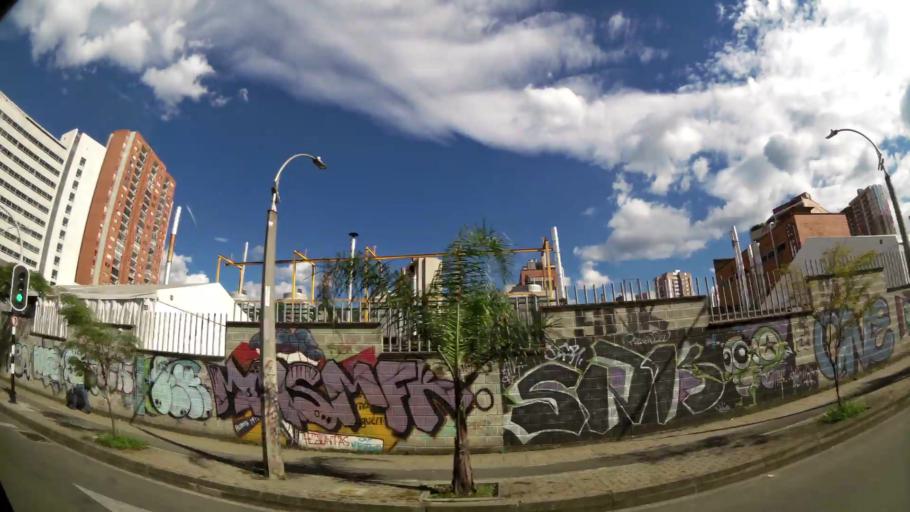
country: CO
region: Antioquia
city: Sabaneta
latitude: 6.1569
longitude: -75.6108
